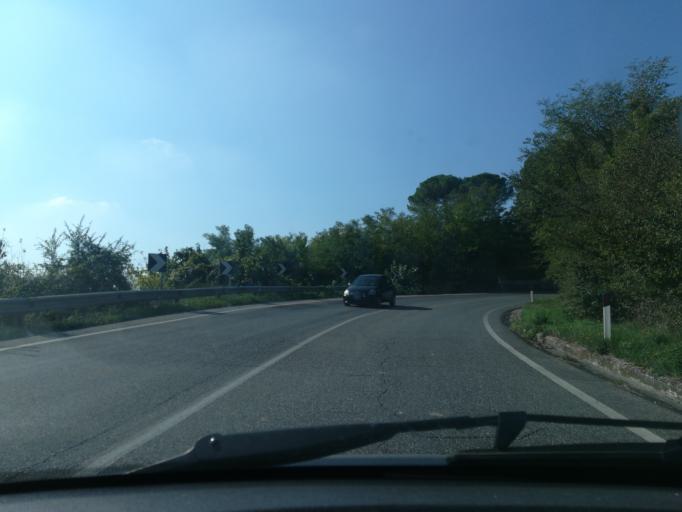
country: IT
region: The Marches
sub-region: Provincia di Macerata
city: Piediripa
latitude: 43.2695
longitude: 13.4694
